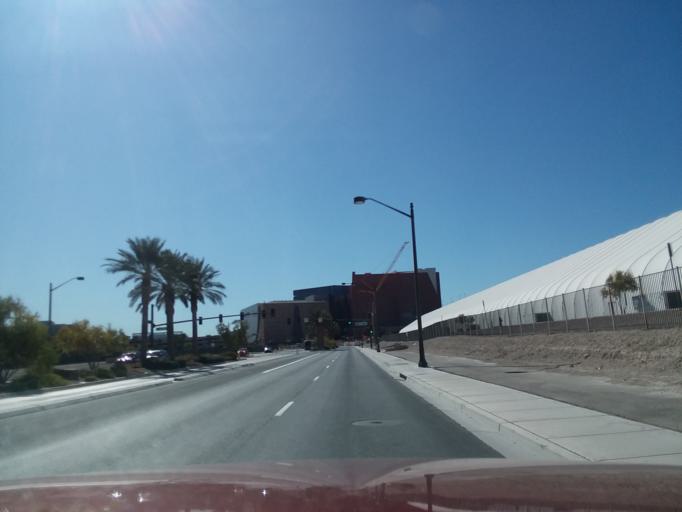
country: US
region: Nevada
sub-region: Clark County
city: Las Vegas
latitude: 36.1729
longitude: -115.1505
